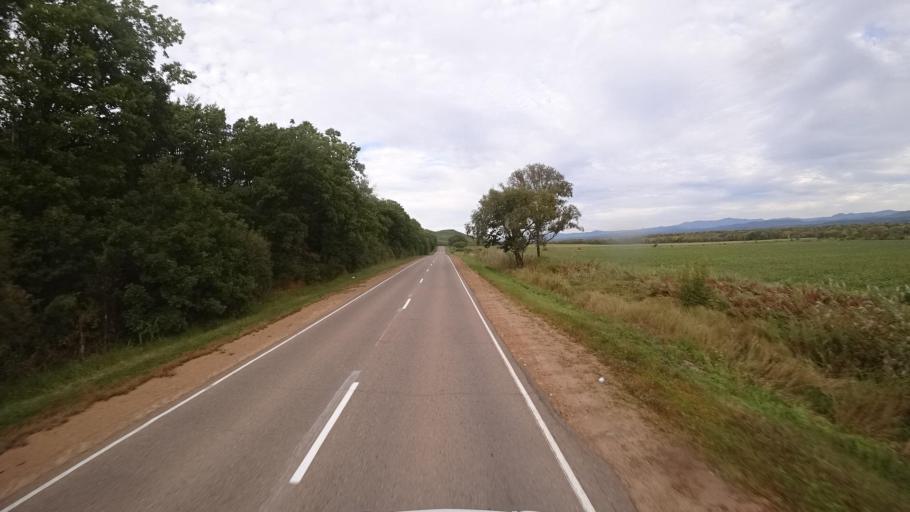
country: RU
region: Primorskiy
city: Dostoyevka
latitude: 44.3725
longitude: 133.4361
